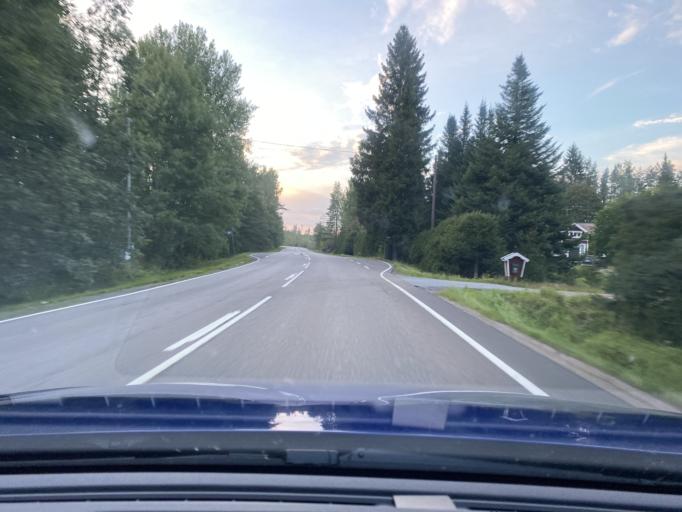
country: FI
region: Satakunta
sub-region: Pohjois-Satakunta
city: Honkajoki
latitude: 61.9368
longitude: 22.2392
